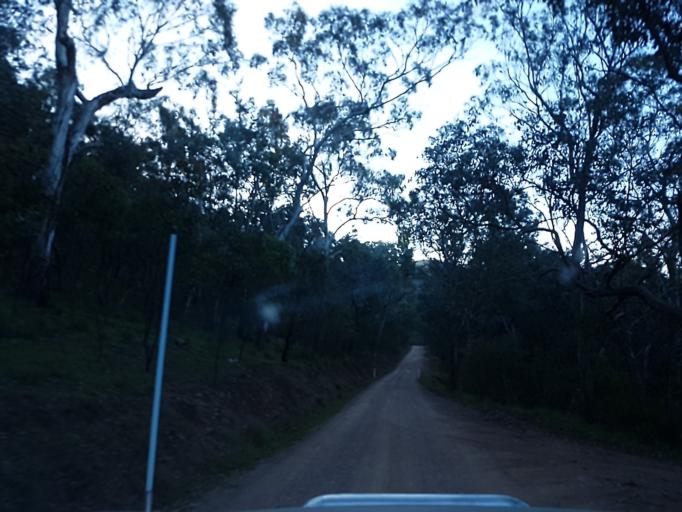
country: AU
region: Victoria
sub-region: Wellington
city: Heyfield
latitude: -37.4066
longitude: 147.0771
